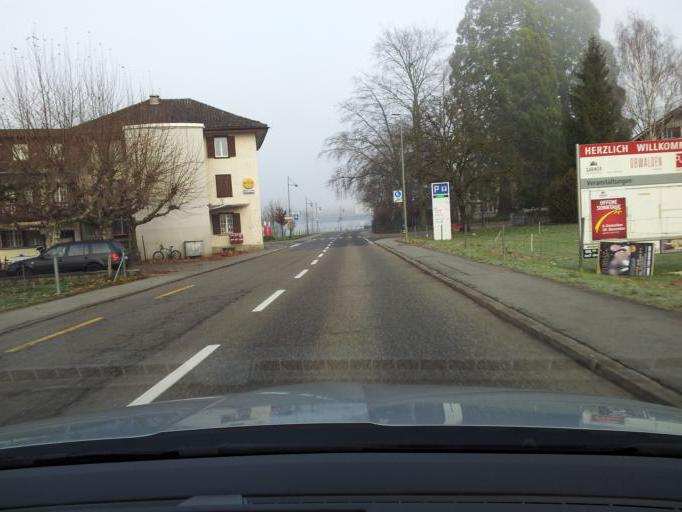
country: CH
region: Obwalden
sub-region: Obwalden
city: Sarnen
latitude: 46.8883
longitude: 8.2454
